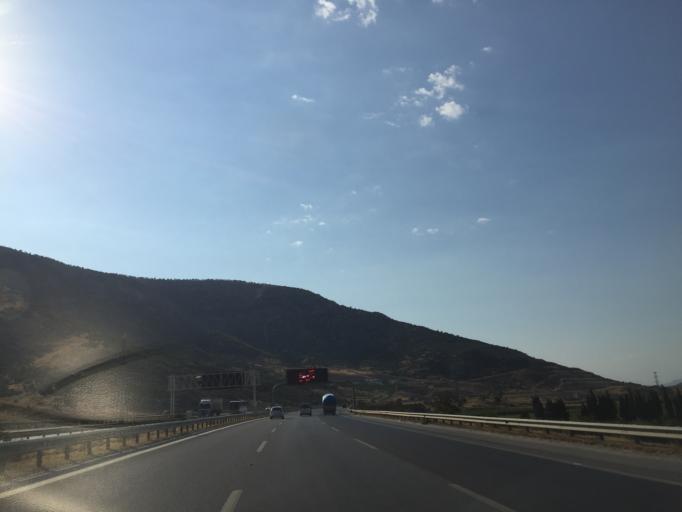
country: TR
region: Izmir
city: Belevi
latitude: 38.0284
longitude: 27.4357
